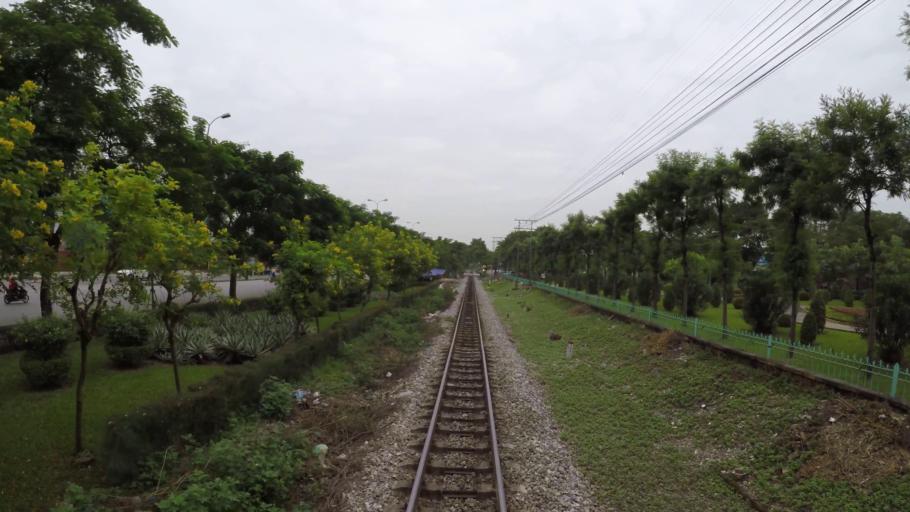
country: VN
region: Hai Phong
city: An Duong
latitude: 20.8767
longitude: 106.6330
